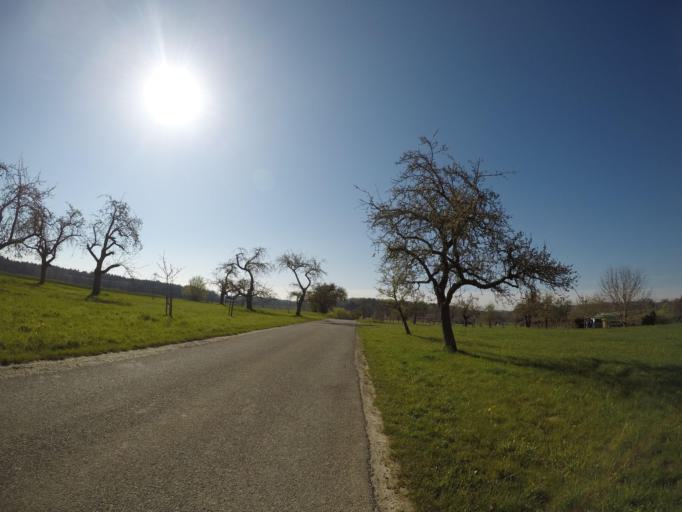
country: DE
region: Baden-Wuerttemberg
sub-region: Tuebingen Region
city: Ebenweiler
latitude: 47.8933
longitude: 9.5232
